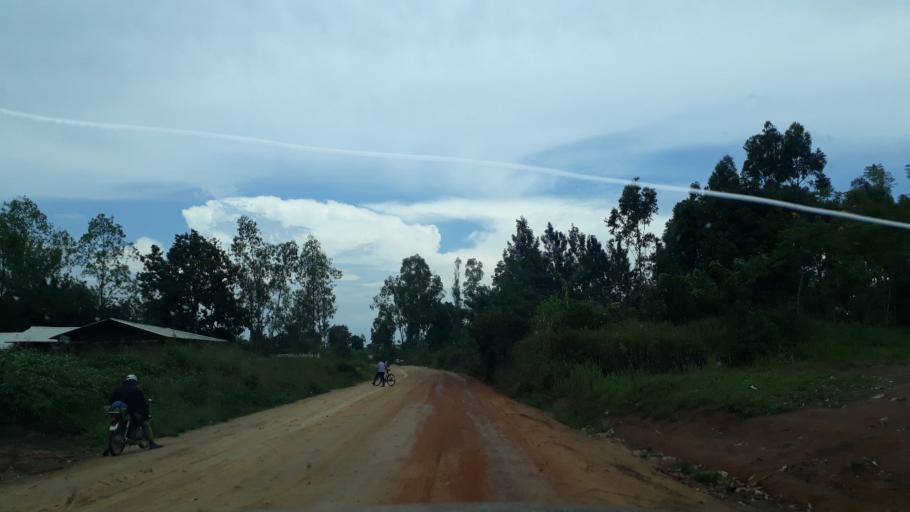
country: CD
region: Eastern Province
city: Bunia
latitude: 1.6091
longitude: 30.2734
